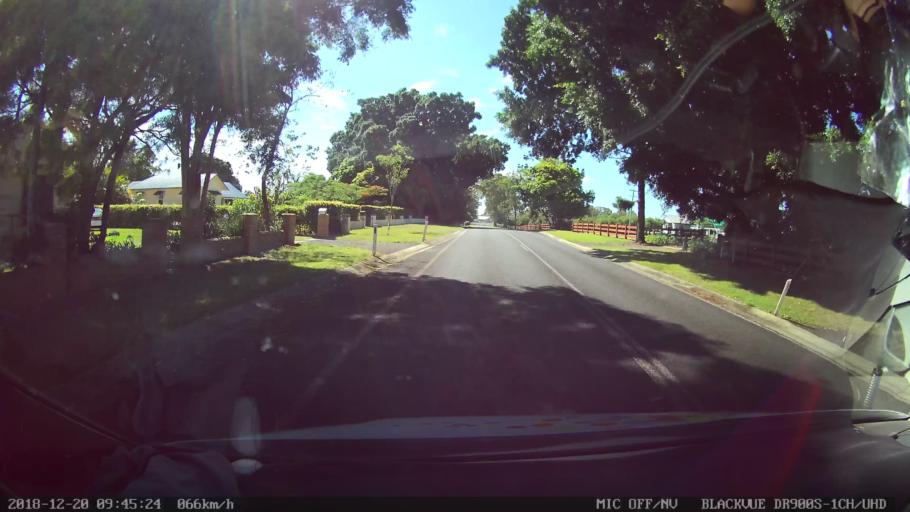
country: AU
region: New South Wales
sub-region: Lismore Municipality
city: Lismore
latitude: -28.7437
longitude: 153.2999
